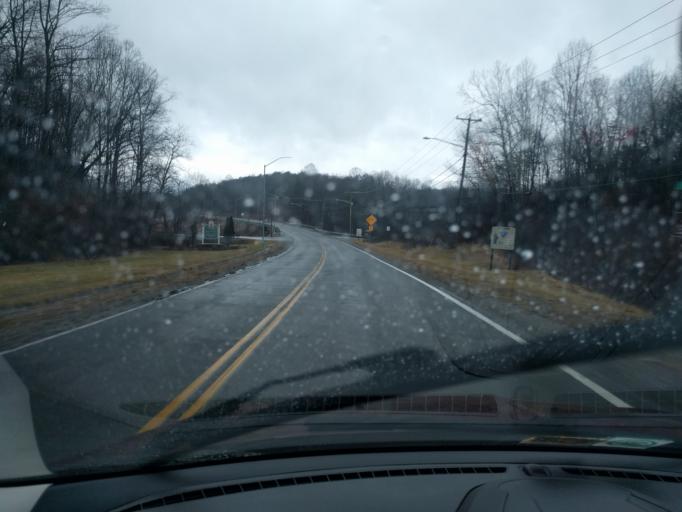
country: US
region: Virginia
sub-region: Pulaski County
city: Pulaski
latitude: 37.0413
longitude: -80.7397
